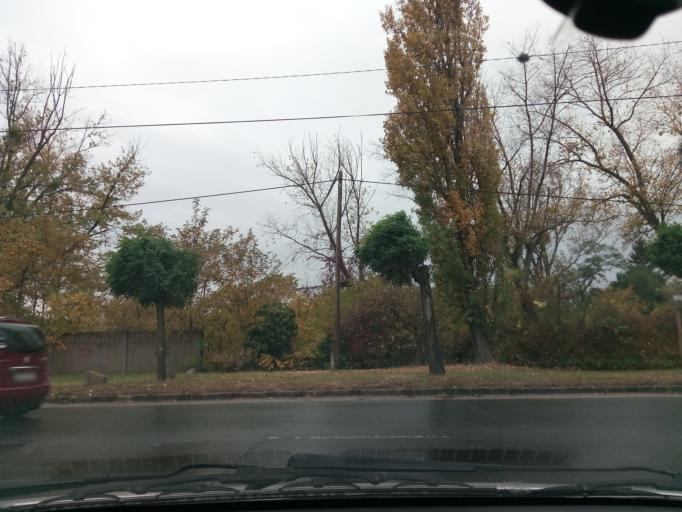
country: HU
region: Pest
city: Gyal
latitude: 47.4256
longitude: 19.2275
